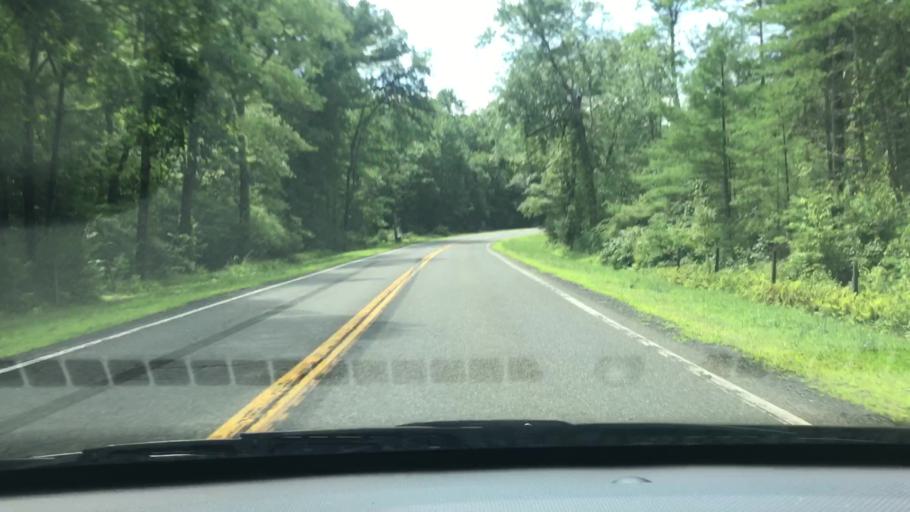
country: US
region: New York
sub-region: Ulster County
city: Shokan
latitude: 41.9643
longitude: -74.2072
